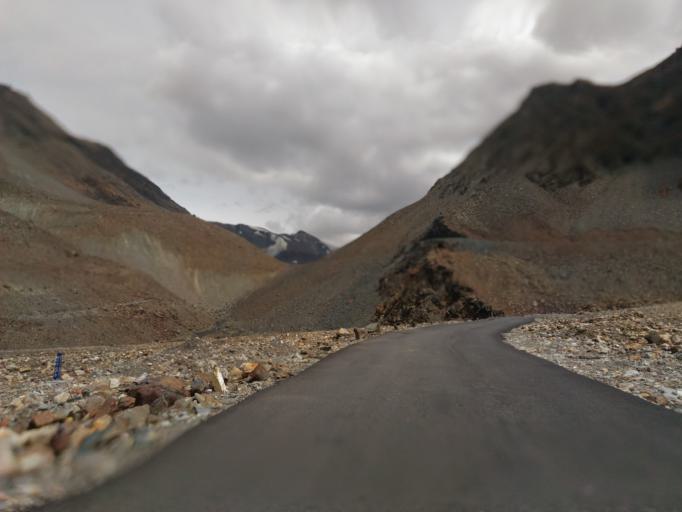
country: IN
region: Himachal Pradesh
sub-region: Lahul and Spiti
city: Kyelang
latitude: 32.7642
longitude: 77.3887
